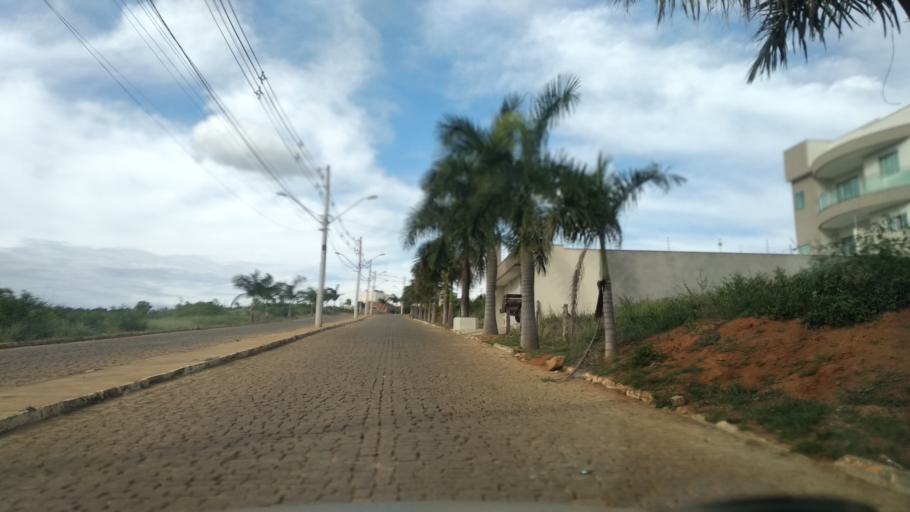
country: BR
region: Bahia
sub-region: Caetite
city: Caetite
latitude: -14.0612
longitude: -42.4961
